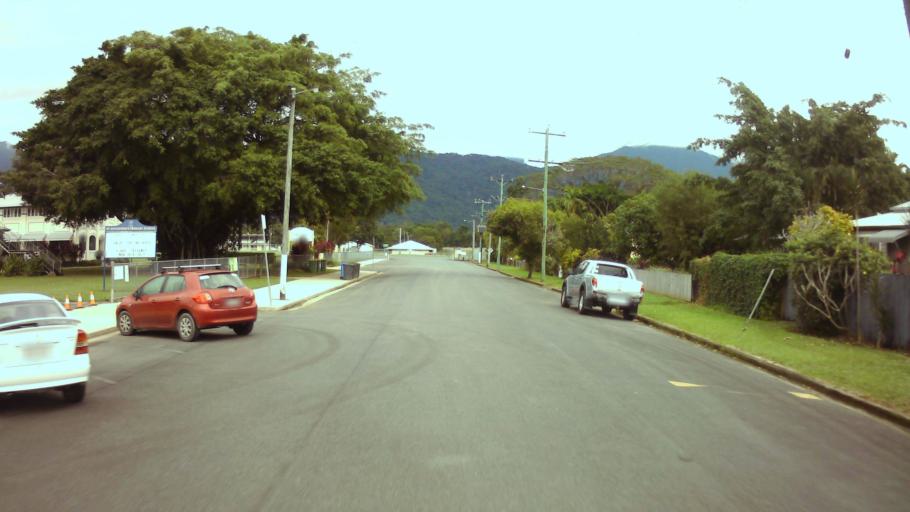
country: AU
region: Queensland
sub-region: Cairns
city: Port Douglas
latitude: -16.4617
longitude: 145.3694
